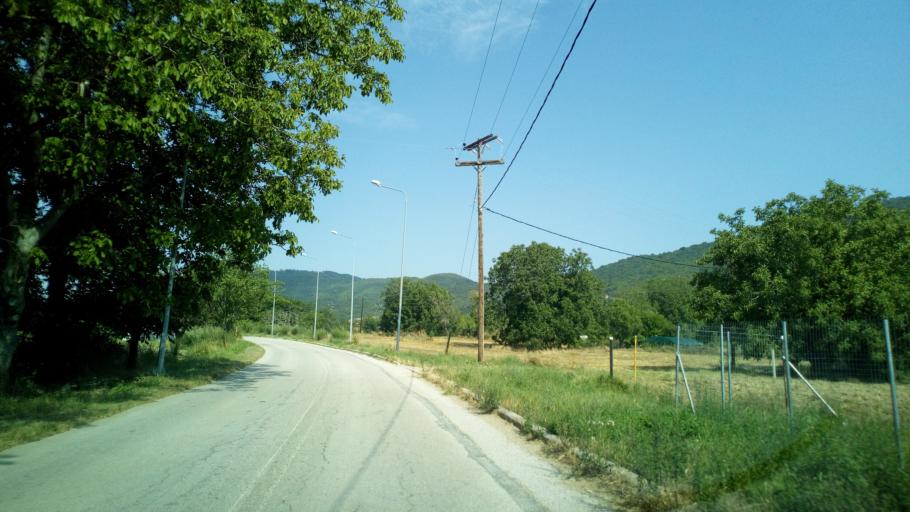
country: GR
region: Central Macedonia
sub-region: Nomos Thessalonikis
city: Sochos
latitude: 40.8117
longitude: 23.3636
